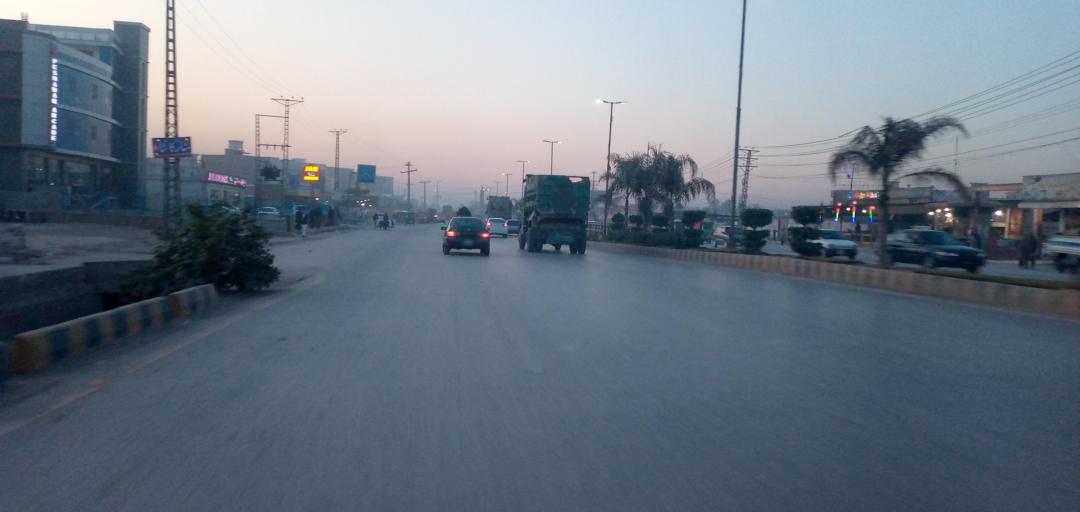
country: PK
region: Khyber Pakhtunkhwa
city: Peshawar
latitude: 34.0308
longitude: 71.6097
